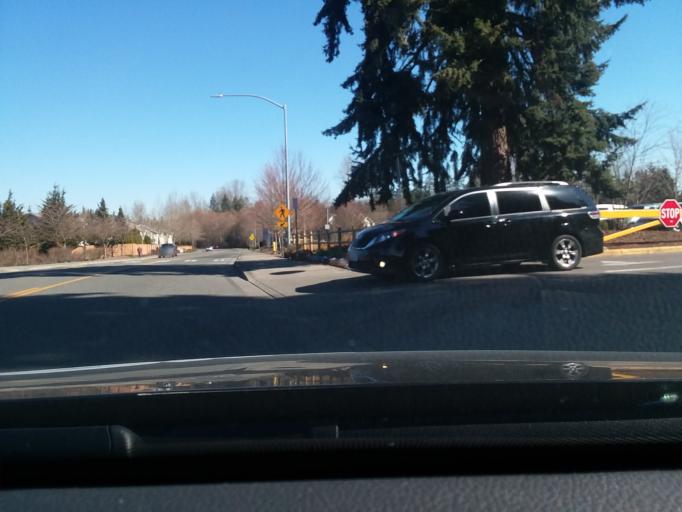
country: US
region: Washington
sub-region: Pierce County
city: Puyallup
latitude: 47.1631
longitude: -122.2873
